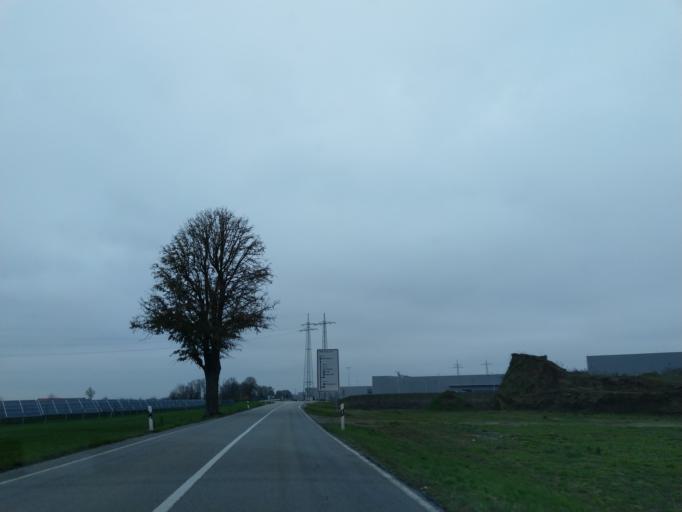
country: DE
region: Bavaria
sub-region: Lower Bavaria
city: Wallersdorf
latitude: 48.7499
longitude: 12.7595
